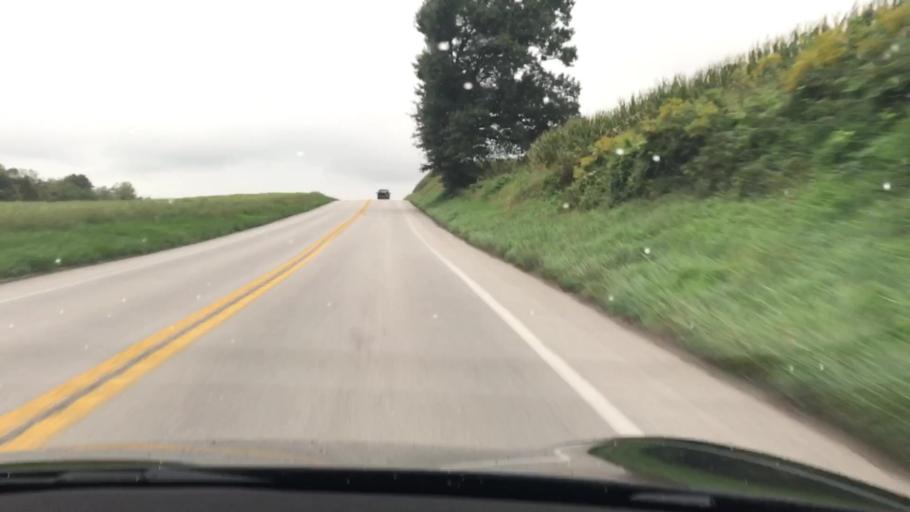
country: US
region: Pennsylvania
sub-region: York County
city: Dover
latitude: 39.9402
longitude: -76.8711
